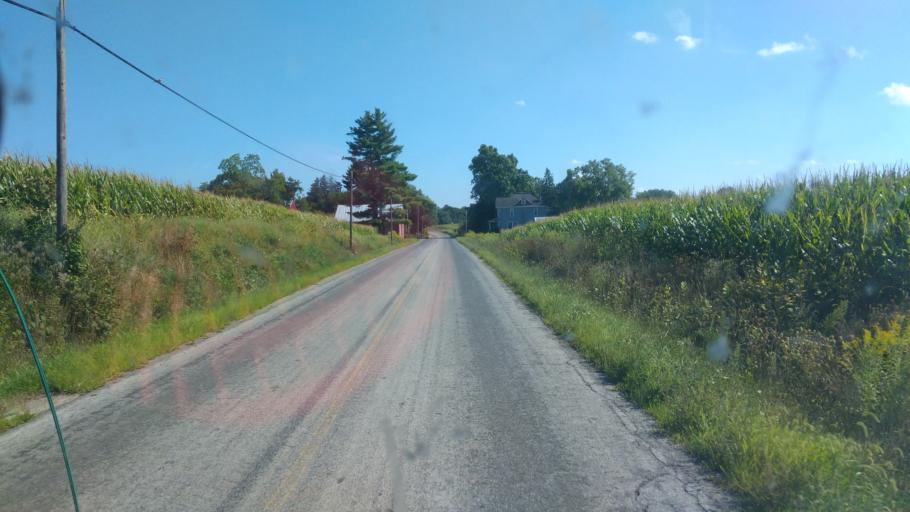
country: US
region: Ohio
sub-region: Ashland County
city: Ashland
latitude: 40.8914
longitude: -82.4282
